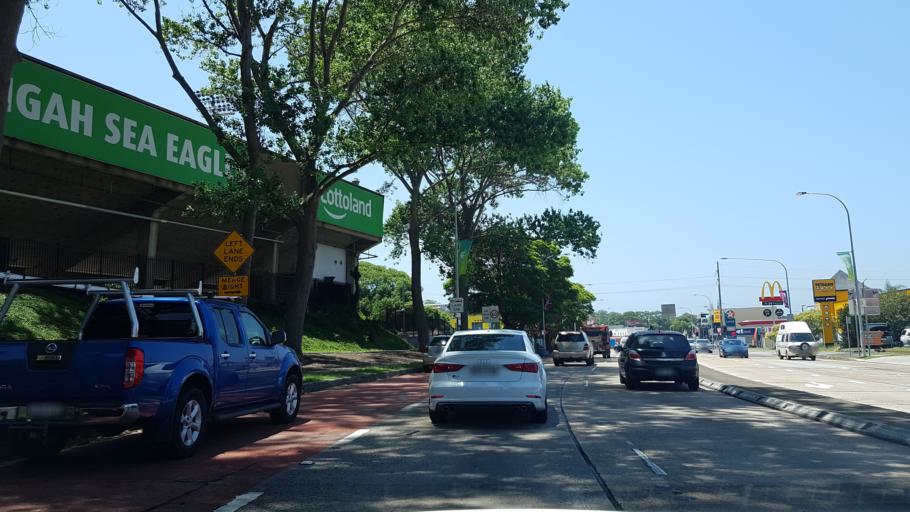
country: AU
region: New South Wales
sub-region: Warringah
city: Brookvale
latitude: -33.7610
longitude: 151.2729
